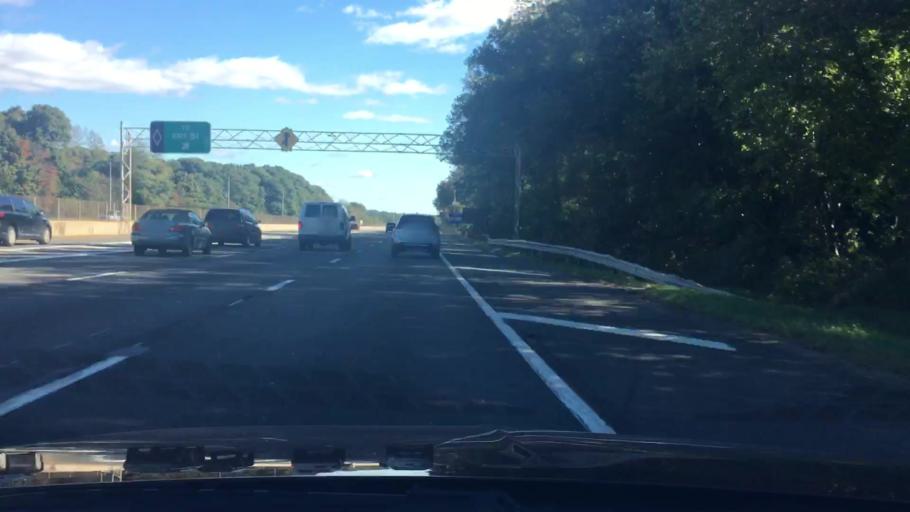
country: US
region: New York
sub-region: Suffolk County
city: Wheatley Heights
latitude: 40.7916
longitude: -73.3621
